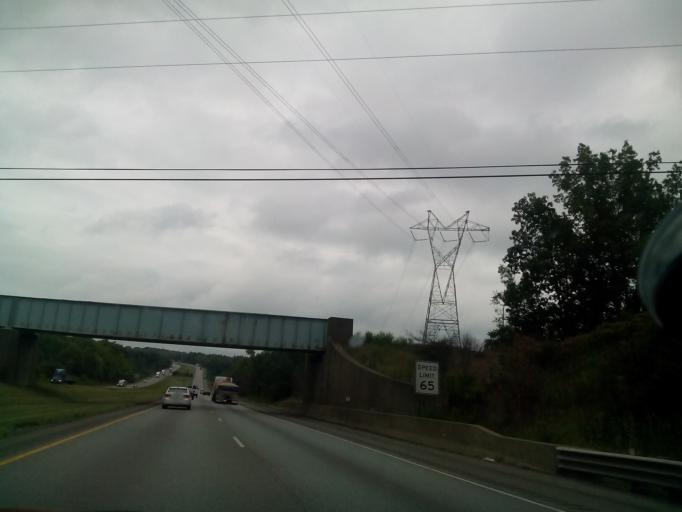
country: US
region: Ohio
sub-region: Trumbull County
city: Hubbard
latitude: 41.1766
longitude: -80.5516
